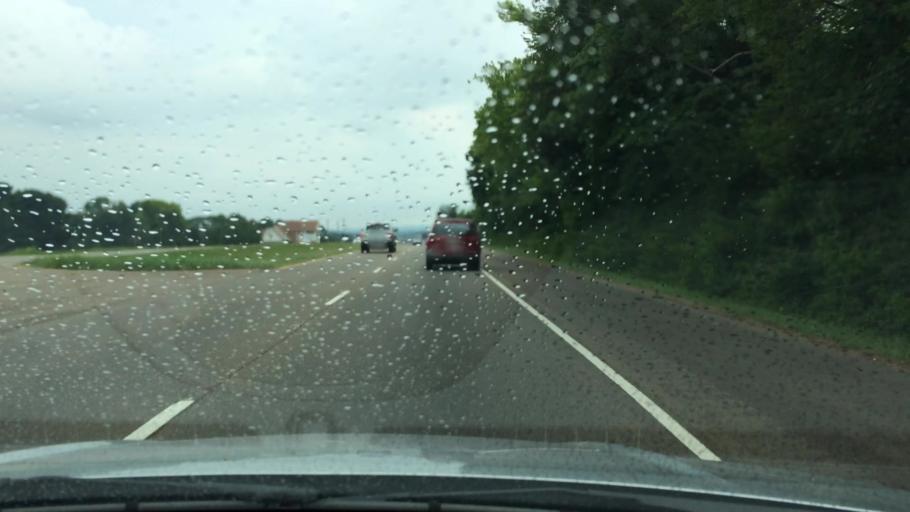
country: US
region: Tennessee
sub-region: Jefferson County
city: Jefferson City
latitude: 36.1123
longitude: -83.5045
